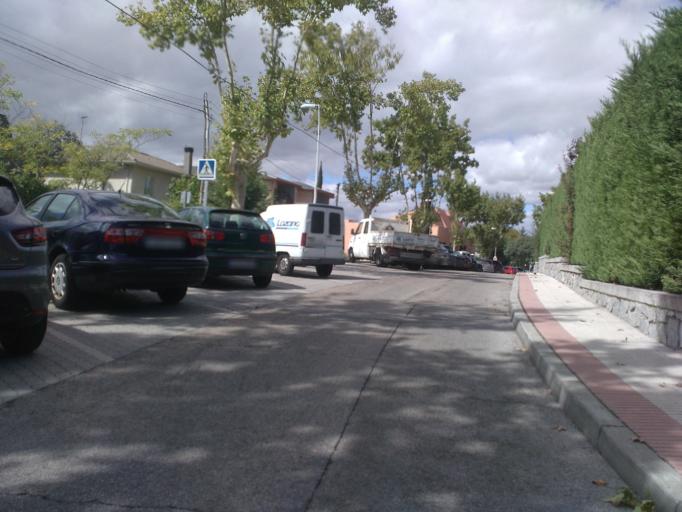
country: ES
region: Madrid
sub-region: Provincia de Madrid
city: Torrelodones
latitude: 40.5774
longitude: -3.9509
